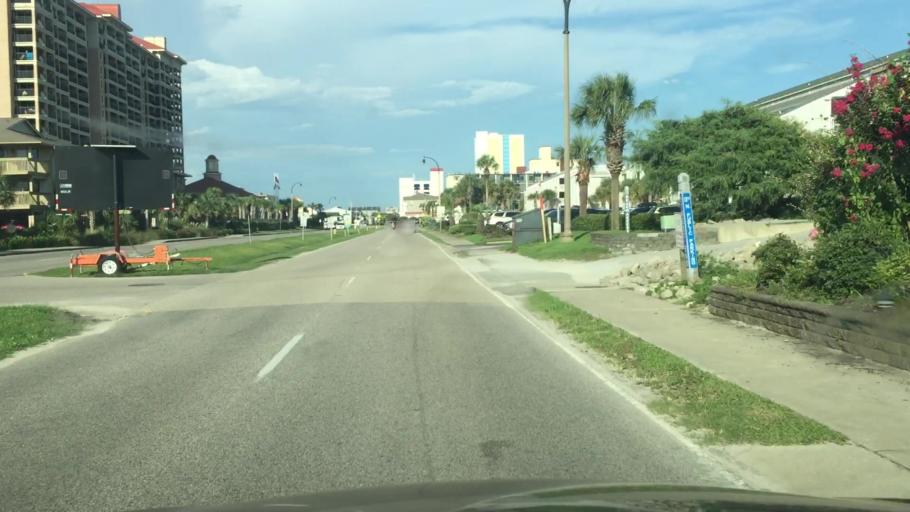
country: US
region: South Carolina
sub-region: Horry County
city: North Myrtle Beach
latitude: 33.8258
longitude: -78.6516
